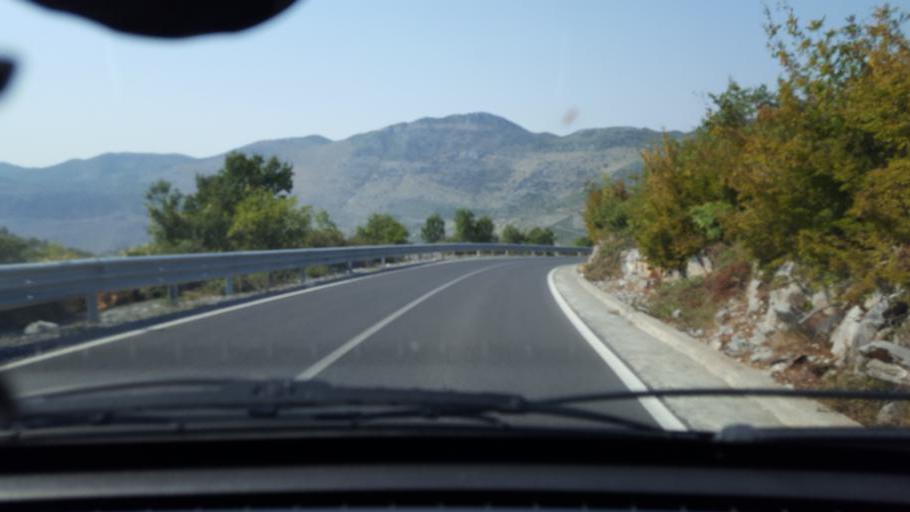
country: AL
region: Shkoder
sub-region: Rrethi i Malesia e Madhe
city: Hot
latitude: 42.3692
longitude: 19.4680
